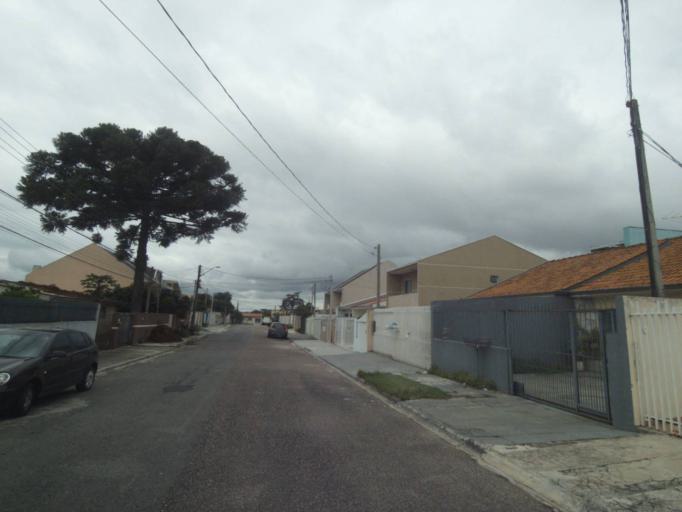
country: BR
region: Parana
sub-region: Pinhais
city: Pinhais
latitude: -25.4537
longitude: -49.2111
